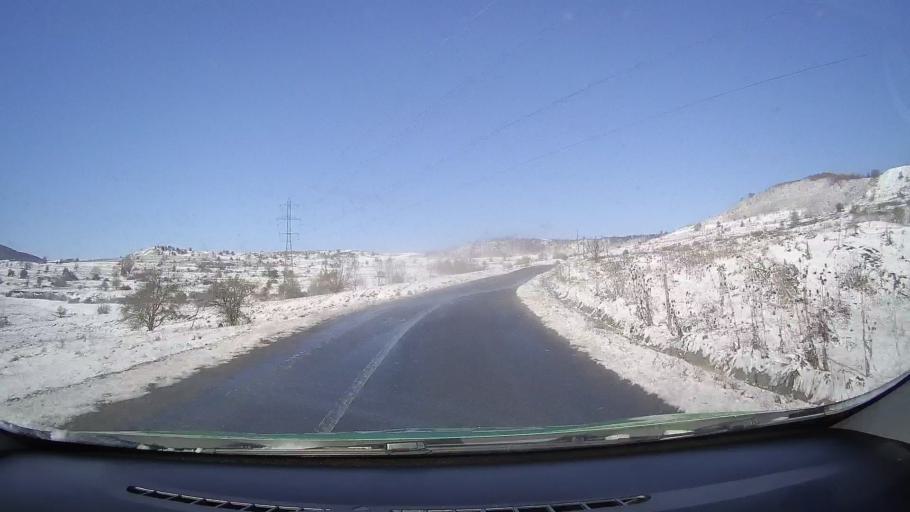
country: RO
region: Sibiu
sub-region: Comuna Avrig
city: Avrig
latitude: 45.7698
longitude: 24.3850
